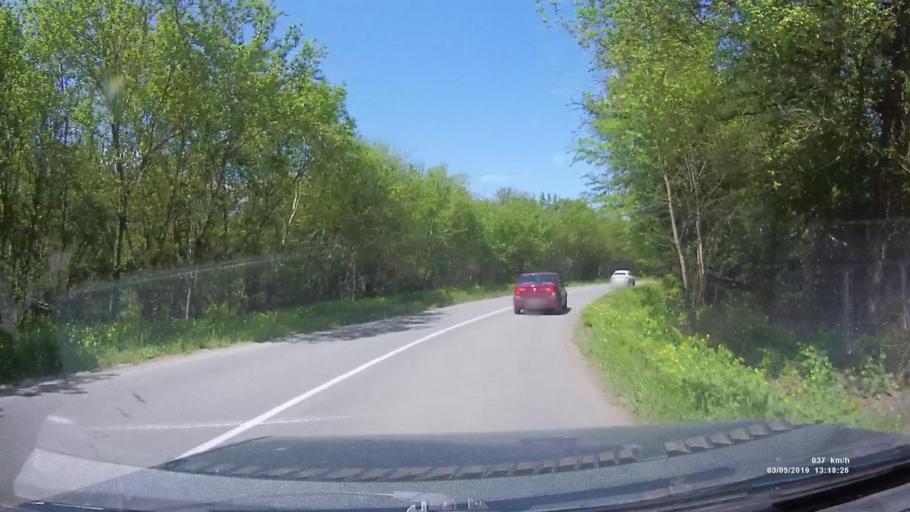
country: RU
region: Rostov
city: Semikarakorsk
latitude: 47.5326
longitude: 40.7483
